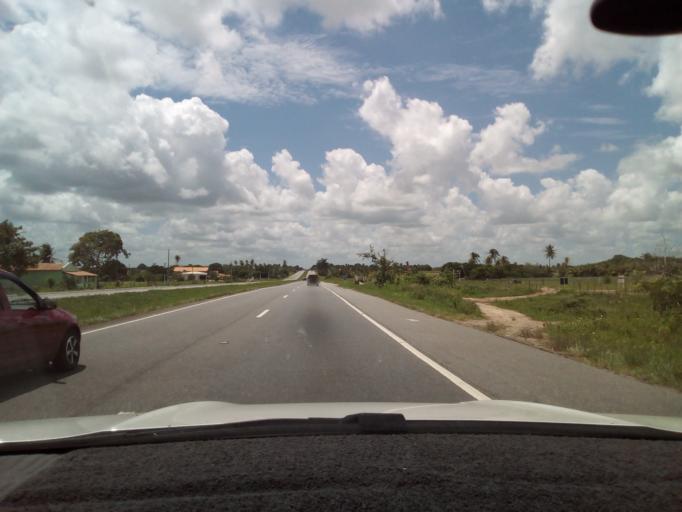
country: BR
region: Paraiba
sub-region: Pilar
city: Pilar
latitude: -7.1822
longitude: -35.3073
